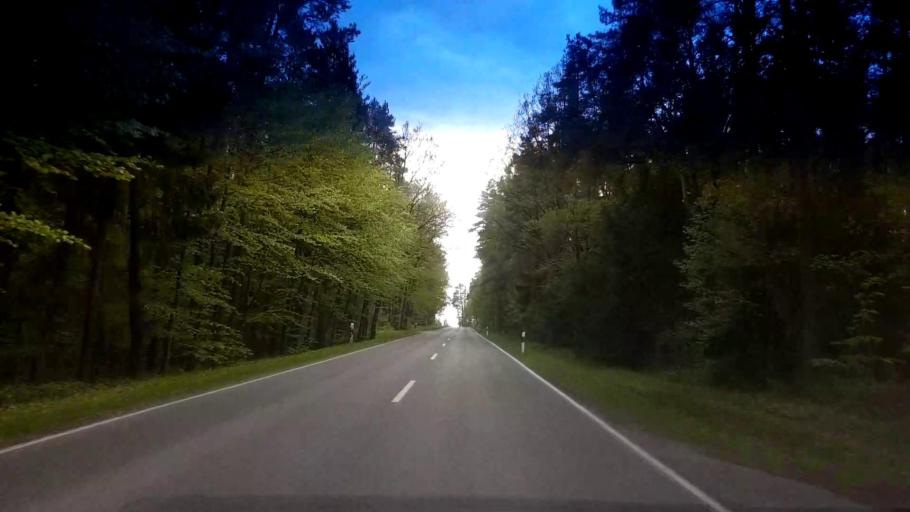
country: DE
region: Bavaria
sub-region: Upper Franconia
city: Pommersfelden
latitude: 49.8014
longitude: 10.8279
